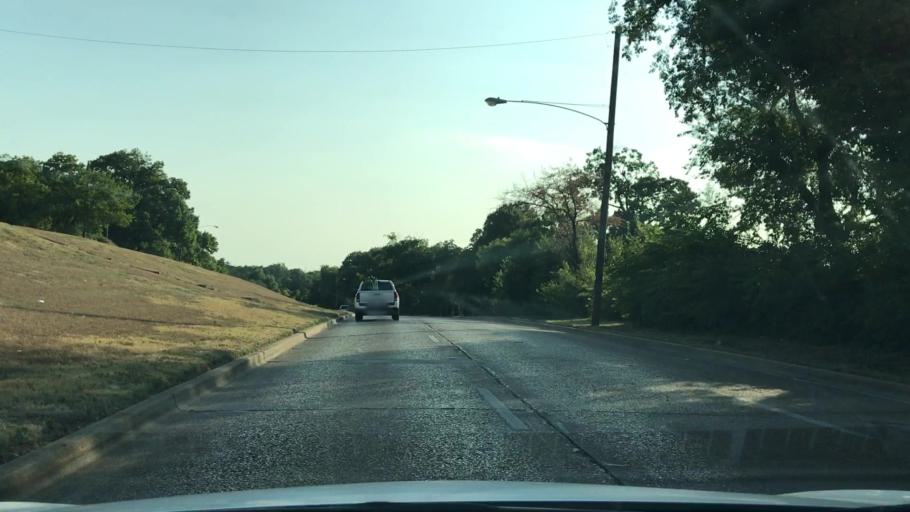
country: US
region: Texas
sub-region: Dallas County
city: Cockrell Hill
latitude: 32.7465
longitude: -96.8655
